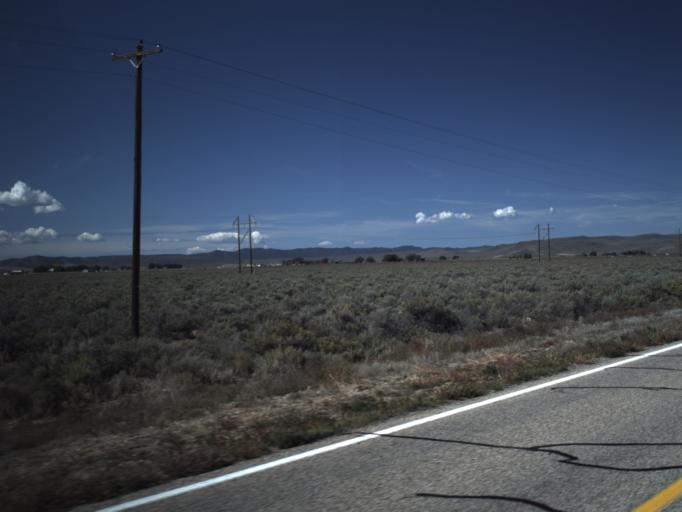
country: US
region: Utah
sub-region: Washington County
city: Enterprise
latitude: 37.7020
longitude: -113.6354
